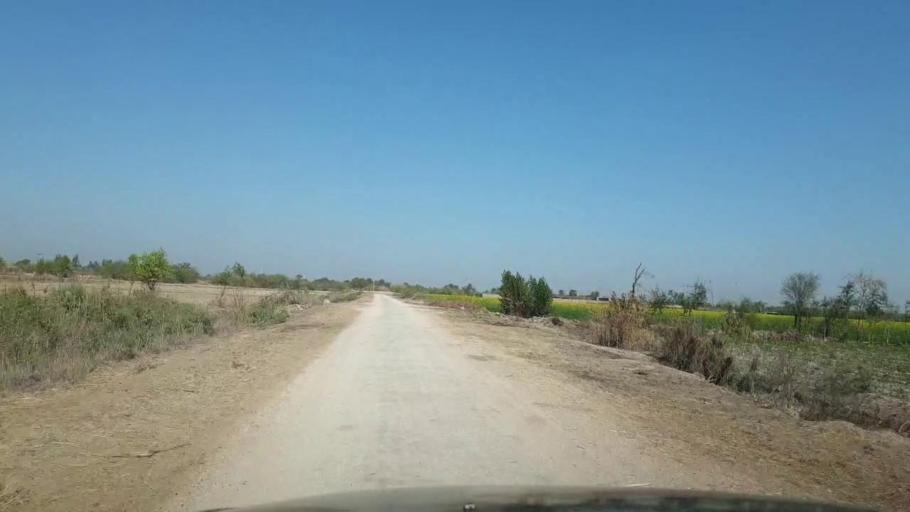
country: PK
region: Sindh
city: Mirpur Khas
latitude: 25.5950
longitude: 69.0683
